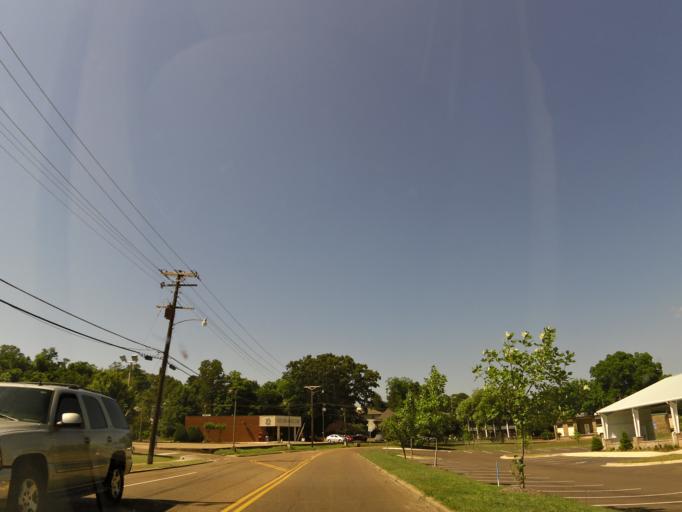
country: US
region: Mississippi
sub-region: Lafayette County
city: Oxford
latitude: 34.3633
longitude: -89.5107
